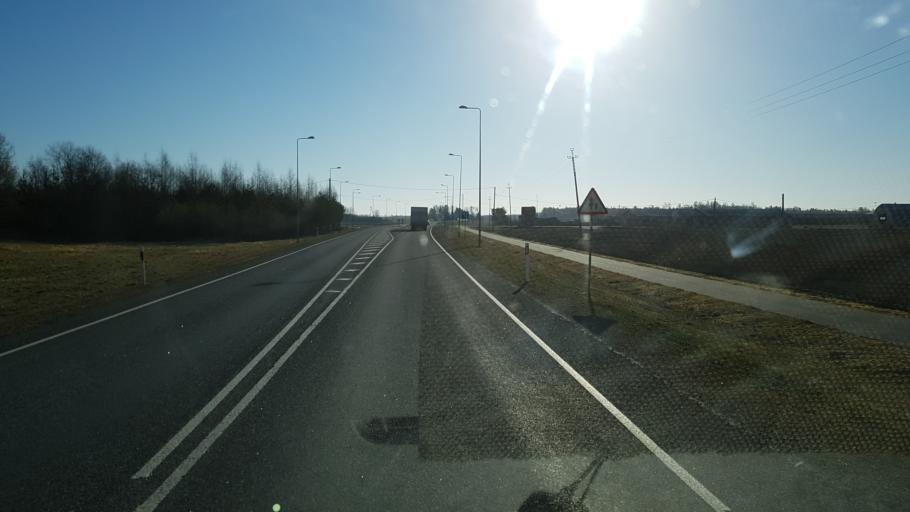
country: EE
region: Jaervamaa
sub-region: Tueri vald
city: Sarevere
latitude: 58.7790
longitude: 25.4773
